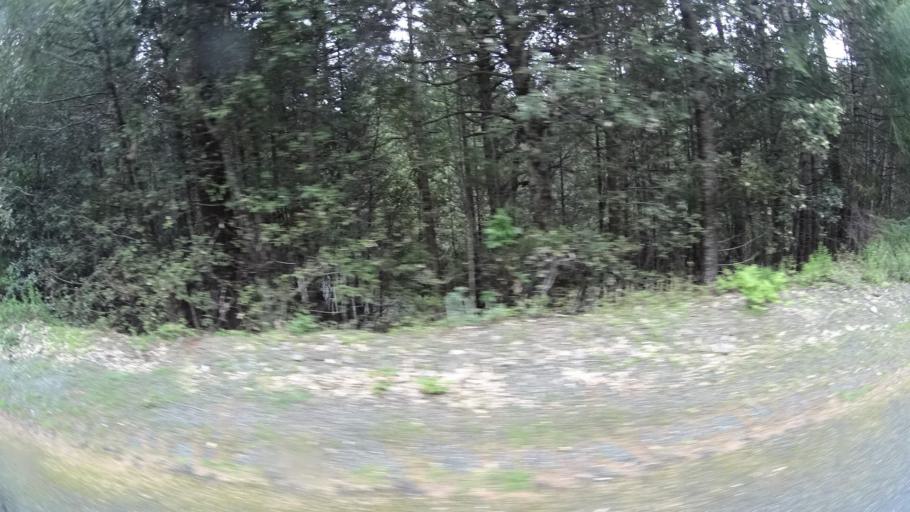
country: US
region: California
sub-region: Humboldt County
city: Willow Creek
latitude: 41.1982
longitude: -123.7782
